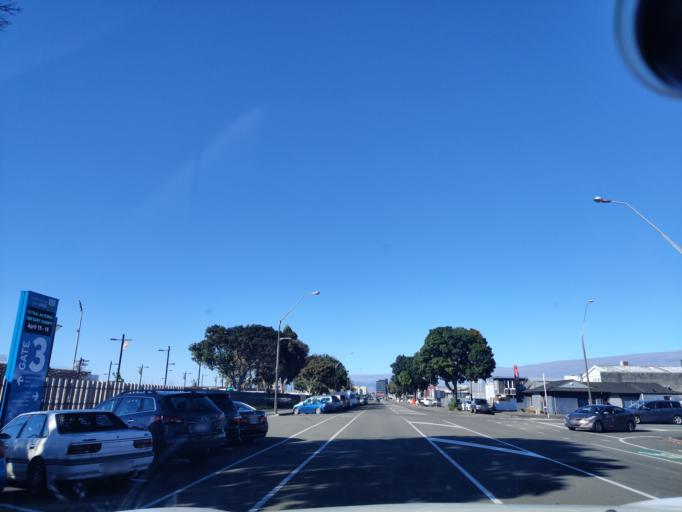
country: NZ
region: Manawatu-Wanganui
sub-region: Palmerston North City
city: Palmerston North
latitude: -40.3585
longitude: 175.6009
